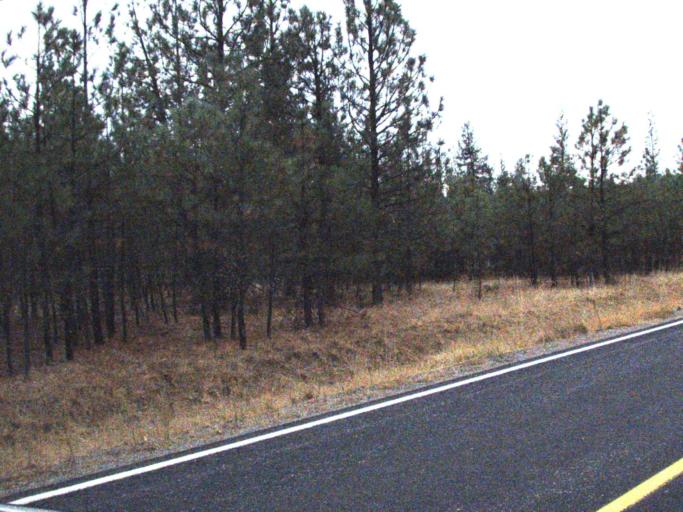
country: US
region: Washington
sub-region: Spokane County
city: Fairchild Air Force Base
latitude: 47.8612
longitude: -117.8444
